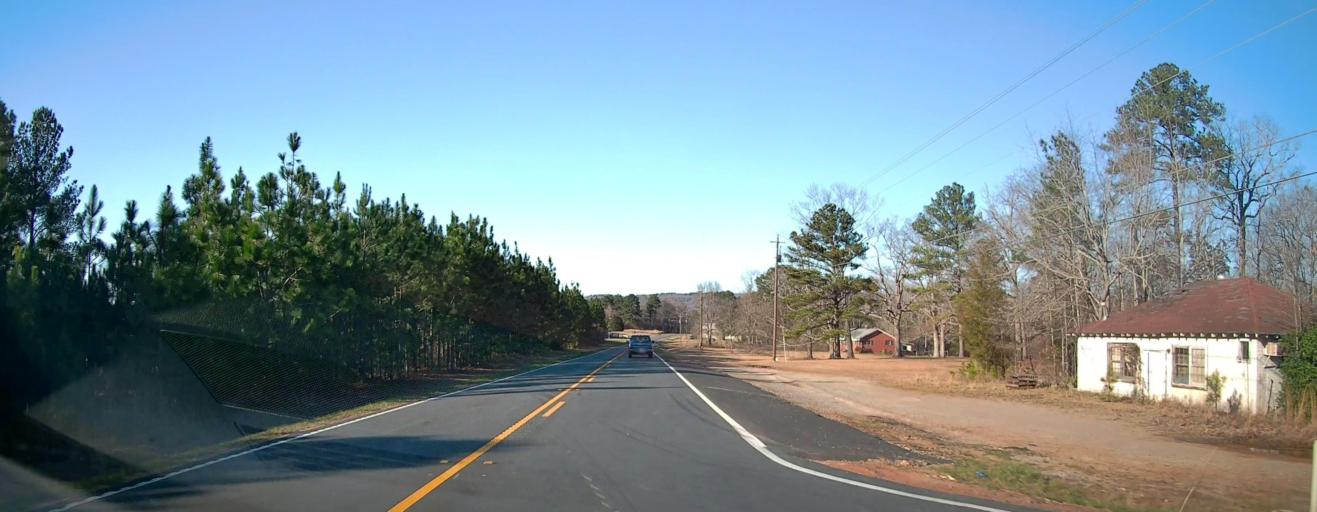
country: US
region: Georgia
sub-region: Talbot County
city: Sardis
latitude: 32.8212
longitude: -84.6987
